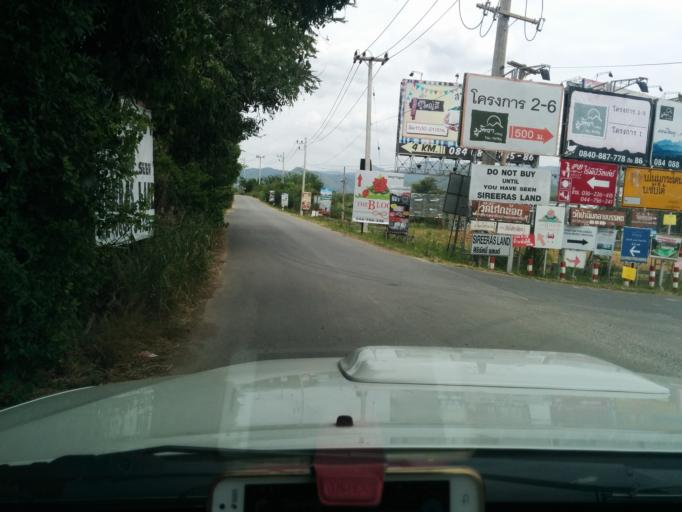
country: TH
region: Sara Buri
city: Muak Lek
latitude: 14.5826
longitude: 101.2270
